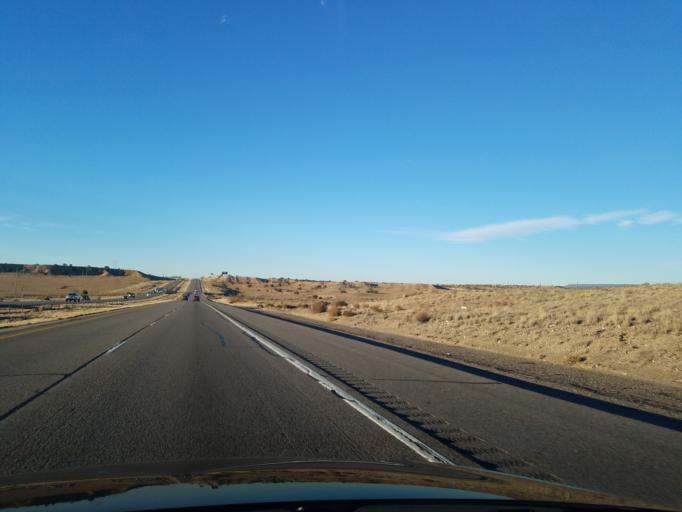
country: US
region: New Mexico
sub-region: Sandoval County
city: San Felipe Pueblo
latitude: 35.4374
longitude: -106.3750
